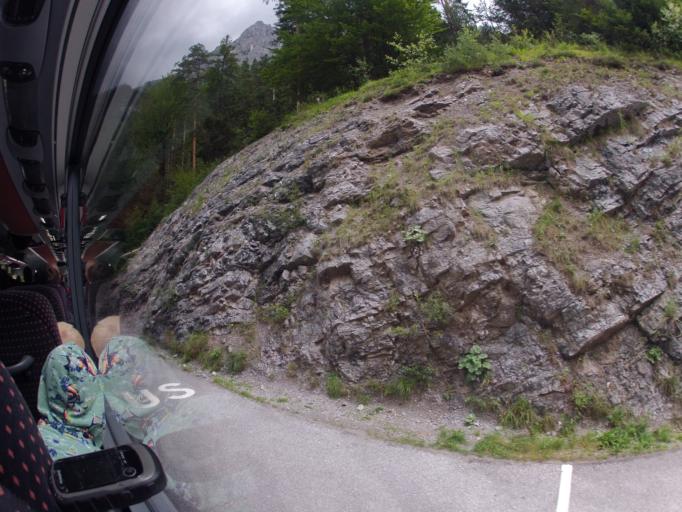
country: AT
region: Salzburg
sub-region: Politischer Bezirk Sankt Johann im Pongau
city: Werfen
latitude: 47.4964
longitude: 13.1957
